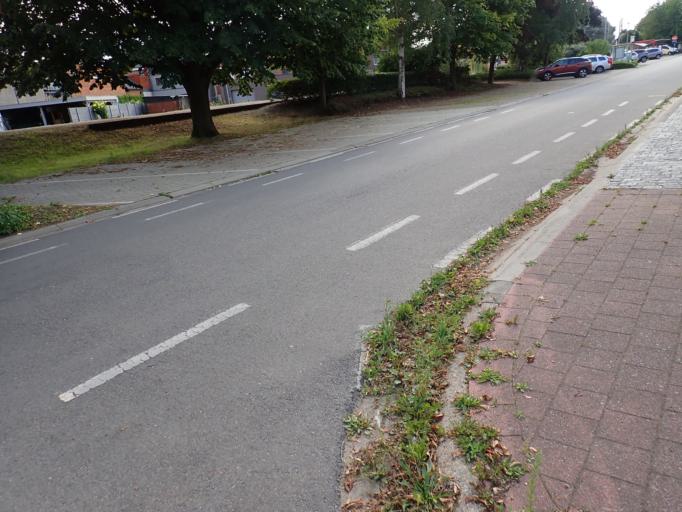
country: BE
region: Flanders
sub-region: Provincie Antwerpen
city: Niel
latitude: 51.0813
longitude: 4.3266
